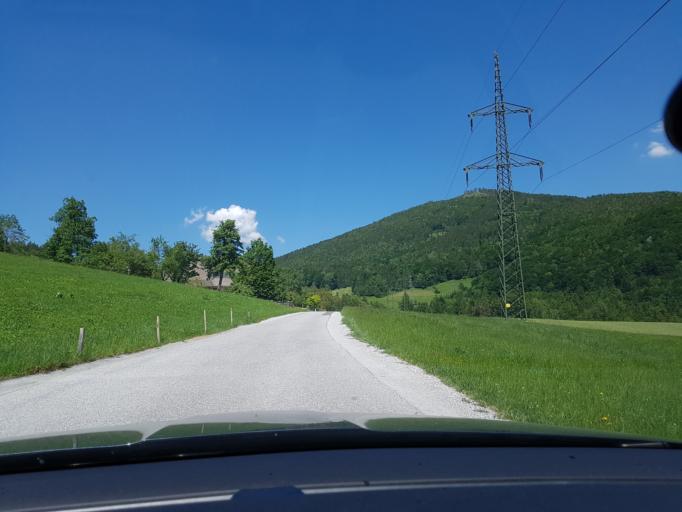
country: AT
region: Salzburg
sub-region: Politischer Bezirk Salzburg-Umgebung
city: Elsbethen
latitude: 47.7788
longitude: 13.1196
